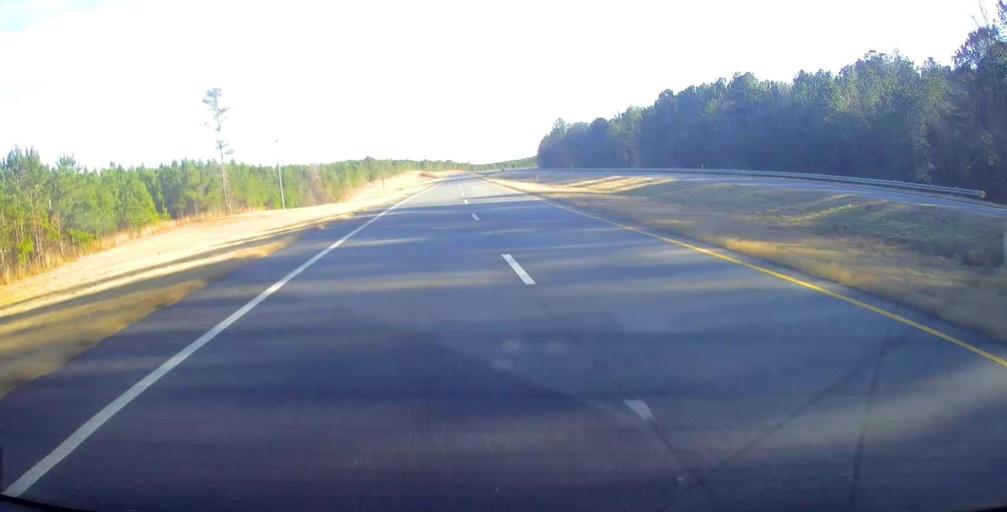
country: US
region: Georgia
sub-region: Upson County
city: Thomaston
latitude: 32.7835
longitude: -84.2462
